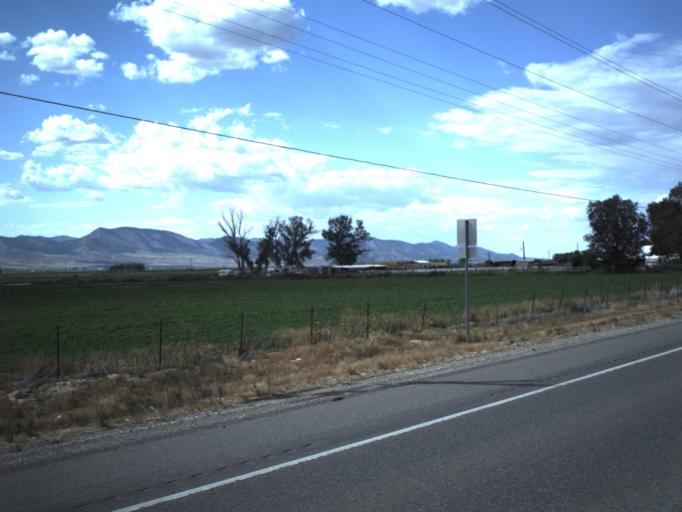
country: US
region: Utah
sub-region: Sanpete County
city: Centerfield
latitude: 39.0895
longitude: -111.8200
